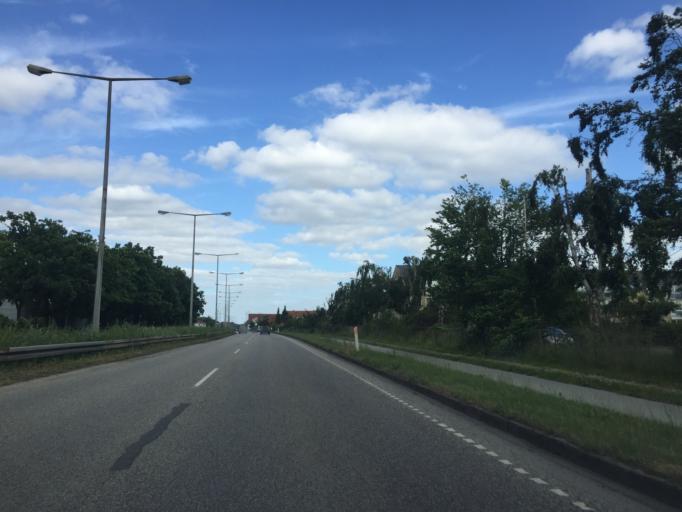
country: DK
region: Capital Region
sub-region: Hoje-Taastrup Kommune
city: Taastrup
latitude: 55.6580
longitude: 12.3011
